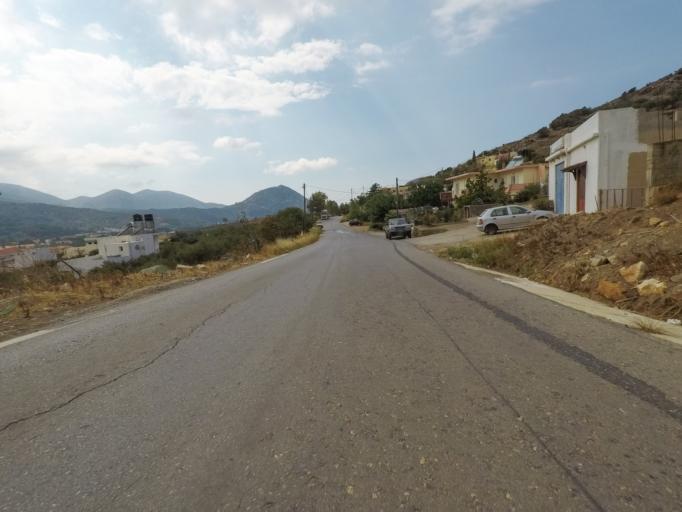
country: GR
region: Crete
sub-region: Nomos Lasithiou
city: Neapoli
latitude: 35.2601
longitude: 25.6121
